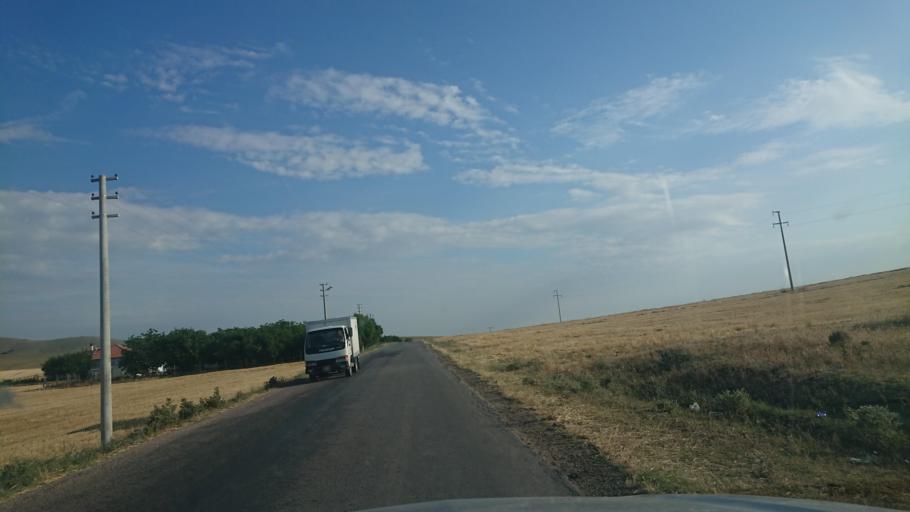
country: TR
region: Aksaray
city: Ortakoy
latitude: 38.7760
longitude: 34.0613
